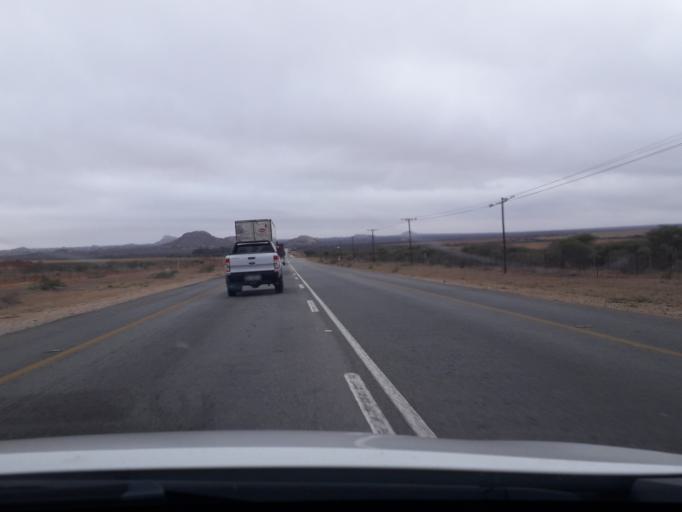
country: ZA
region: Limpopo
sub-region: Capricorn District Municipality
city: Mankoeng
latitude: -23.5588
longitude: 29.6848
